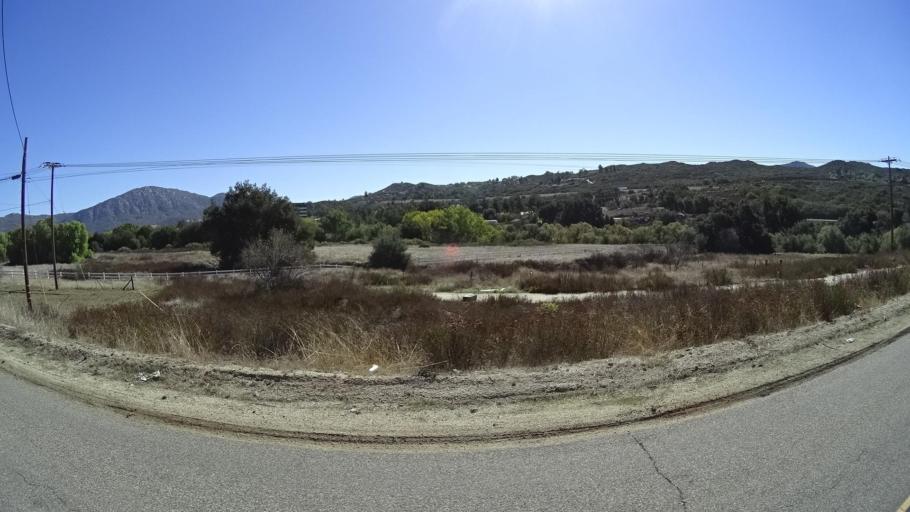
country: US
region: California
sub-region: San Diego County
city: Alpine
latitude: 32.8419
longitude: -116.7118
